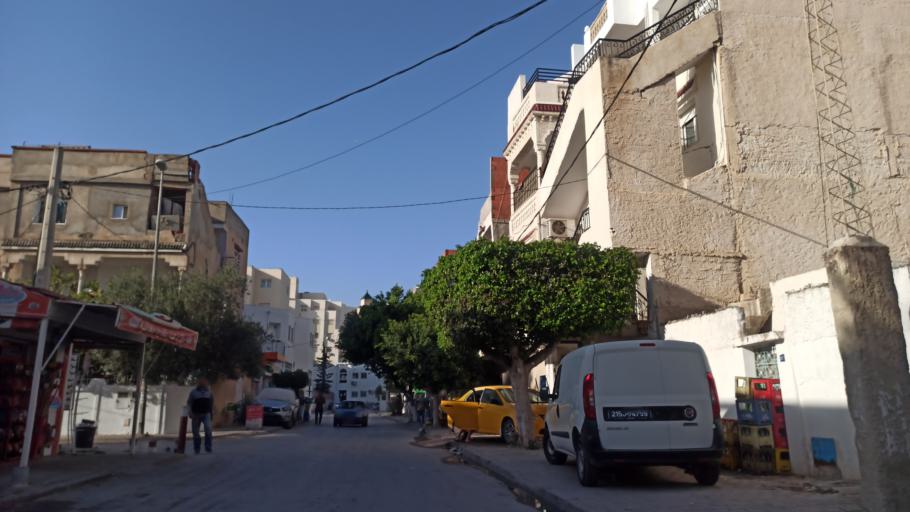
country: TN
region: Tunis
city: La Goulette
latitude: 36.8551
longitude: 10.2701
